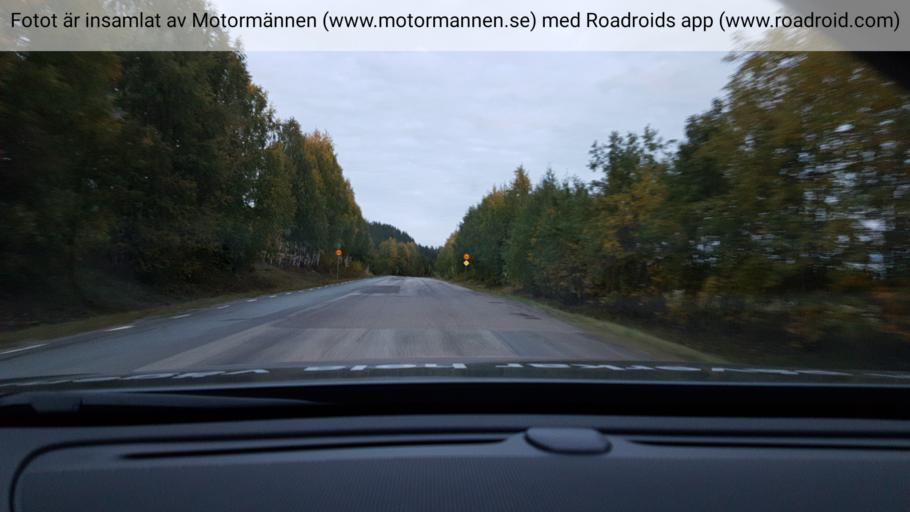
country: SE
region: Norrbotten
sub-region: Alvsbyns Kommun
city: AElvsbyn
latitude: 65.8532
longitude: 20.4395
